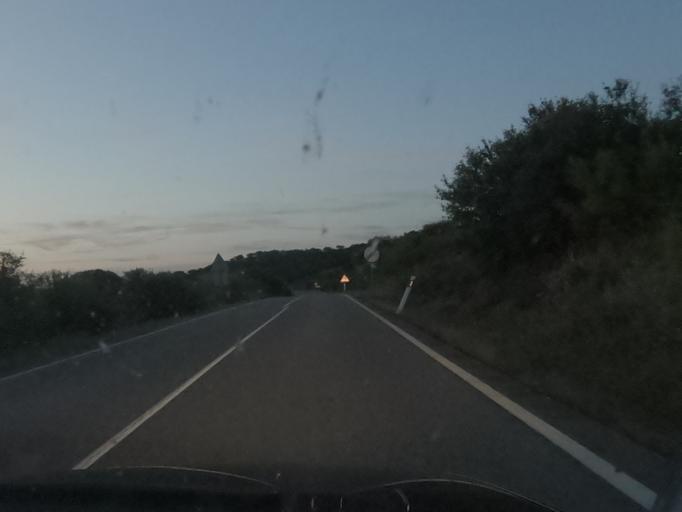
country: ES
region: Extremadura
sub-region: Provincia de Caceres
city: Piedras Albas
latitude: 39.7901
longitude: -6.9578
